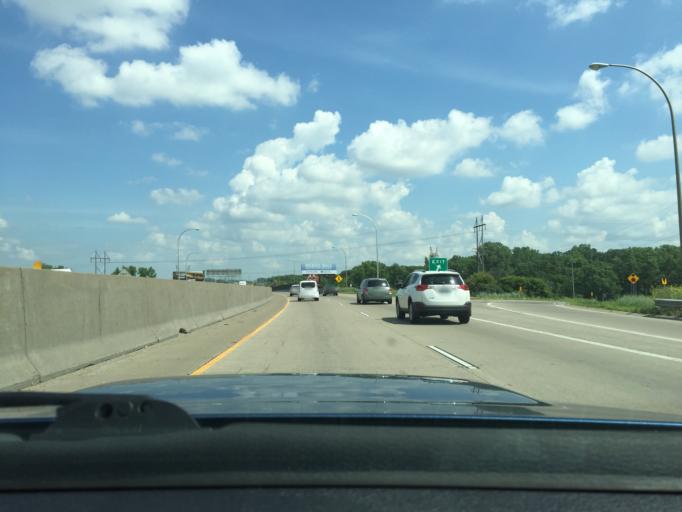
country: US
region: Minnesota
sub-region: Ramsey County
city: Lauderdale
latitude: 44.9748
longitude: -93.2023
